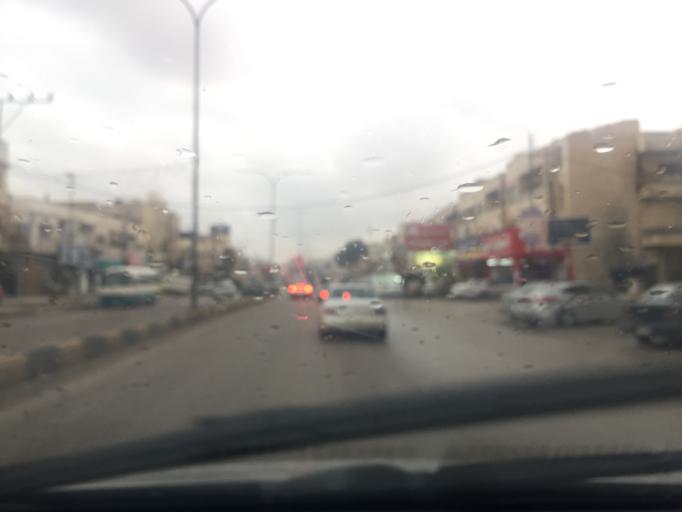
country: JO
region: Zarqa
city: Russeifa
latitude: 32.0279
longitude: 36.0365
